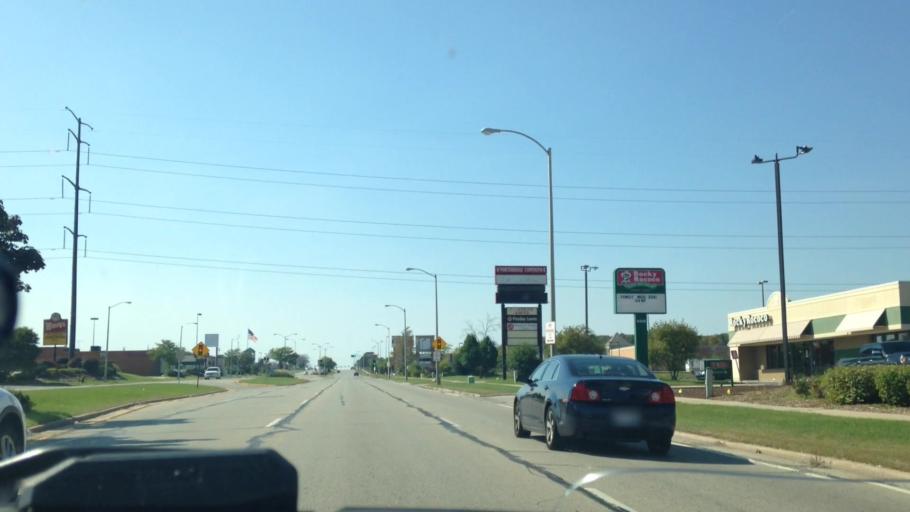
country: US
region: Wisconsin
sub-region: Milwaukee County
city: Brown Deer
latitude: 43.1779
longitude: -88.0125
